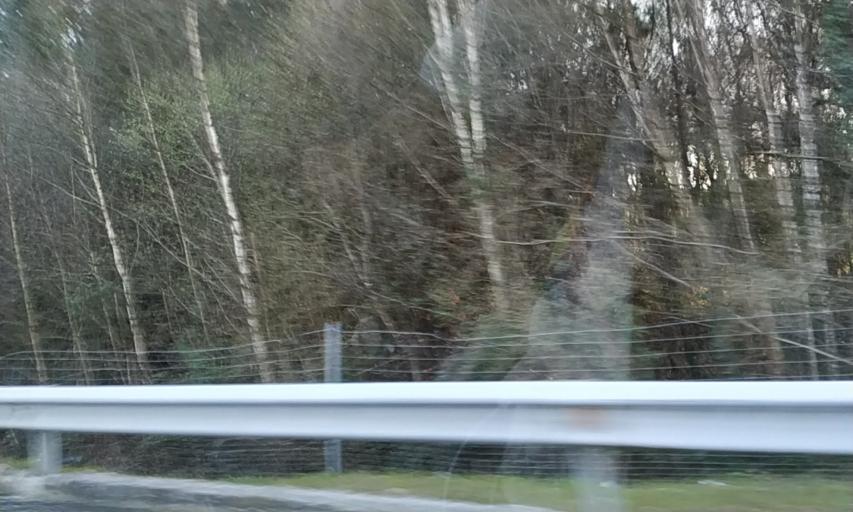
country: ES
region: Galicia
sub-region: Provincia de Lugo
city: Corgo
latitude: 42.9362
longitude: -7.3853
